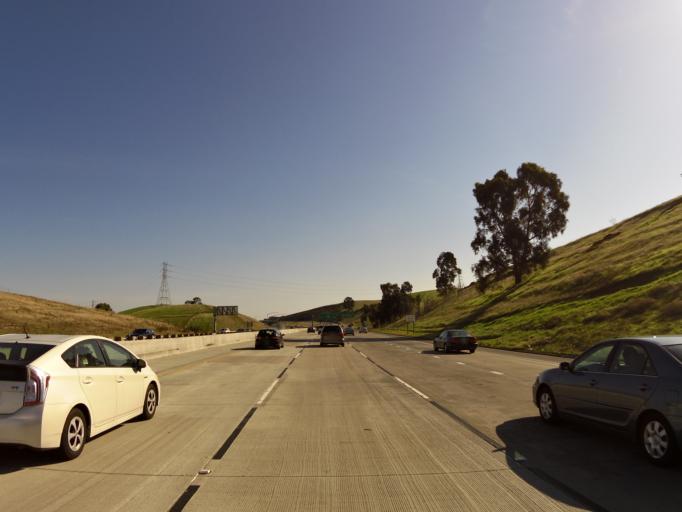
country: US
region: California
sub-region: Contra Costa County
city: Antioch
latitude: 37.9928
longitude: -121.7687
